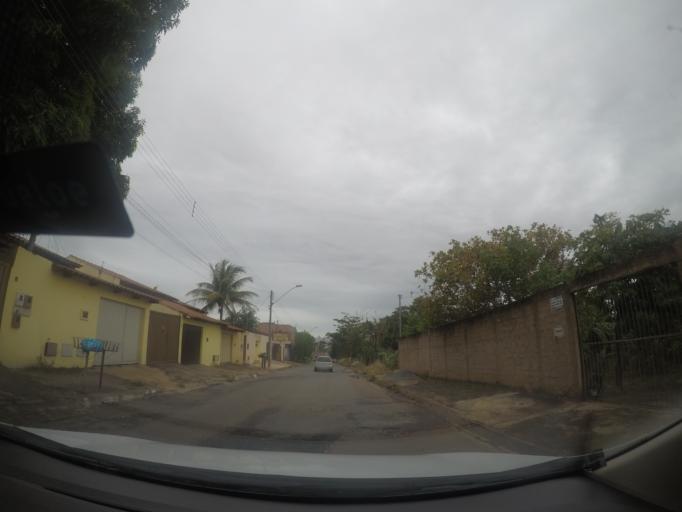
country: BR
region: Goias
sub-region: Goiania
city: Goiania
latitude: -16.6709
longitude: -49.3276
